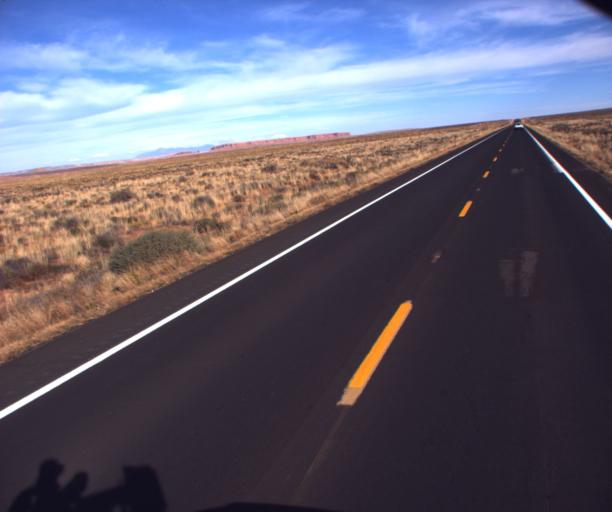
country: US
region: Arizona
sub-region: Apache County
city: Lukachukai
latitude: 36.9637
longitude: -109.4712
